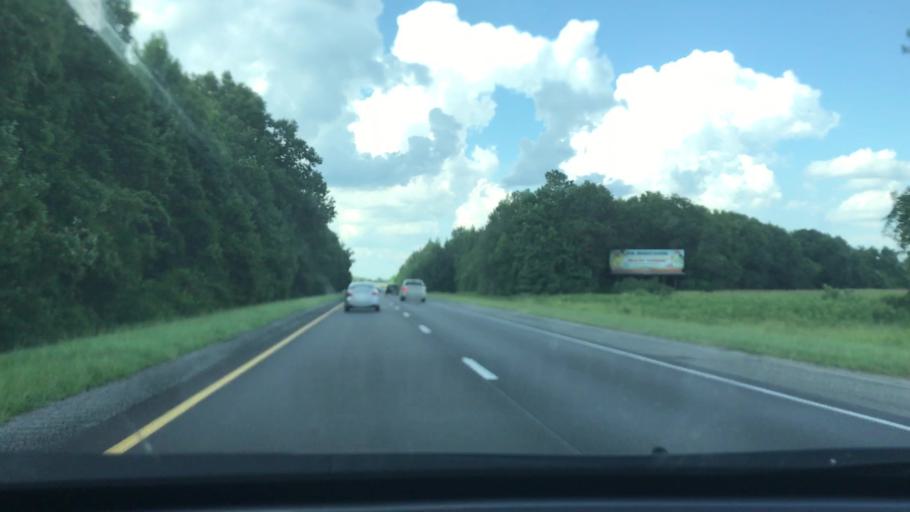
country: US
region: South Carolina
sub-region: Clarendon County
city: Manning
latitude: 33.8511
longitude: -80.1183
